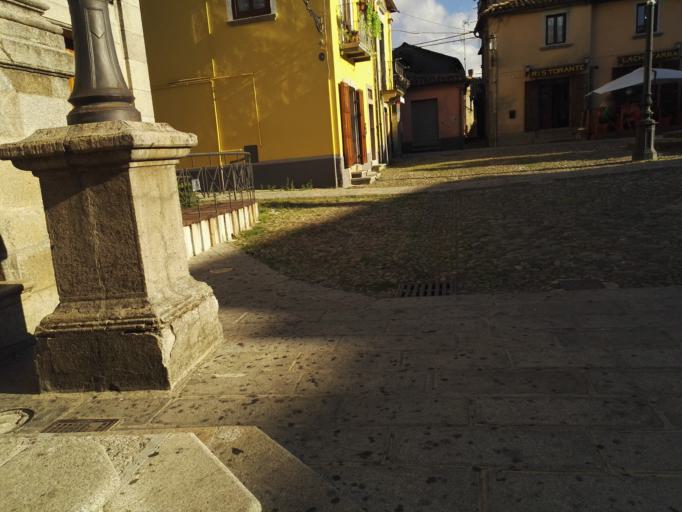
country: IT
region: Calabria
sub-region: Provincia di Vibo-Valentia
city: Serra San Bruno
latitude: 38.5795
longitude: 16.3326
